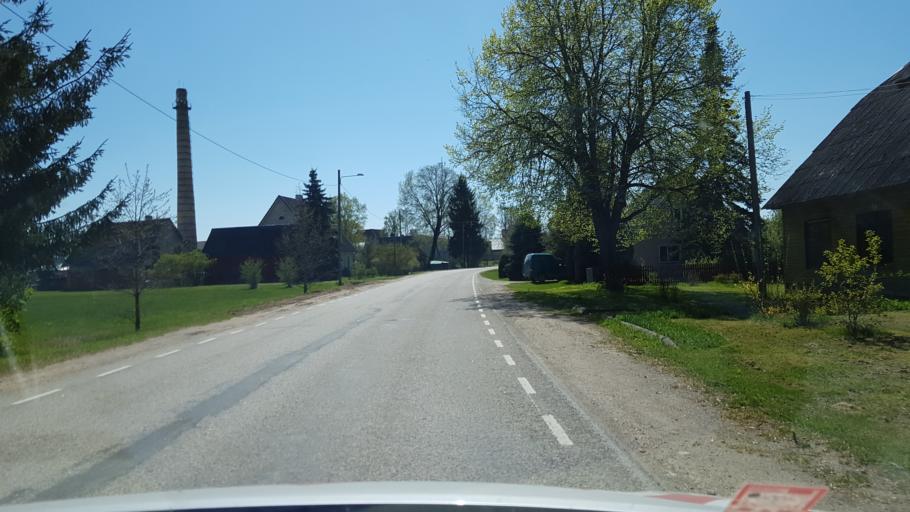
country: EE
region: Vorumaa
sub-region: Antsla vald
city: Vana-Antsla
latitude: 57.8220
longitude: 26.5236
